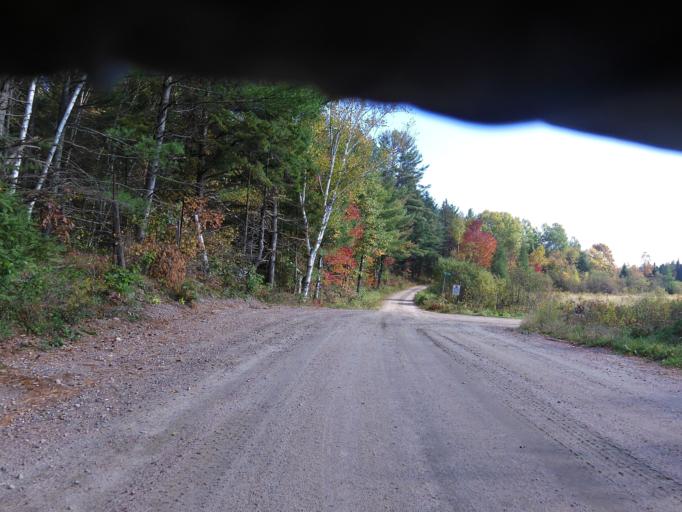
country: CA
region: Ontario
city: Petawawa
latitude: 45.8006
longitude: -77.3186
